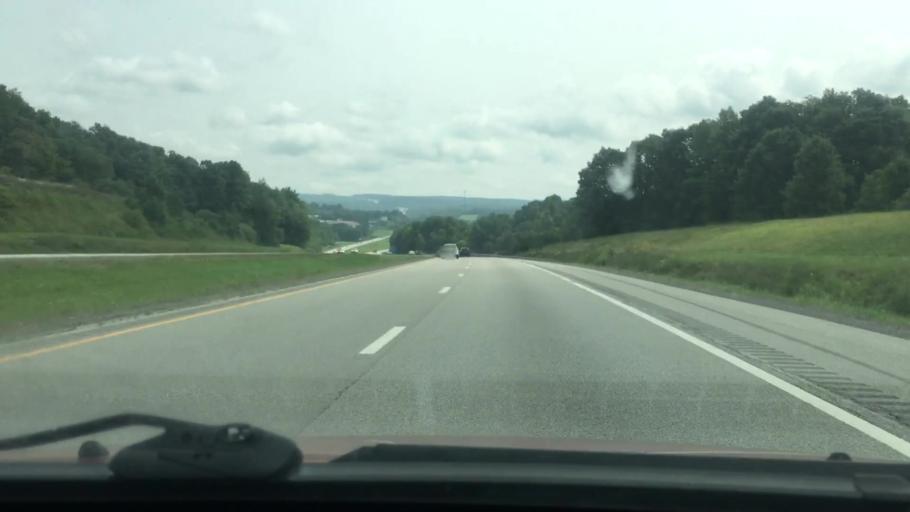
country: US
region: West Virginia
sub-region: Preston County
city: Terra Alta
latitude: 39.6567
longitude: -79.5682
